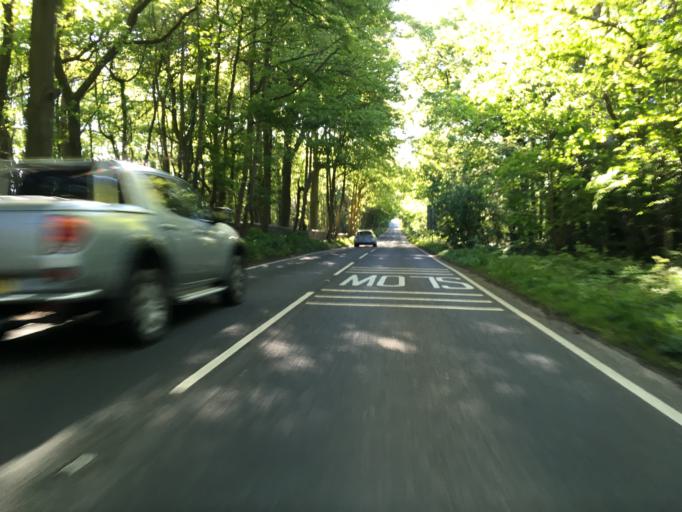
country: GB
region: England
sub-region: North Somerset
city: Easton-in-Gordano
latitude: 51.4494
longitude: -2.7252
